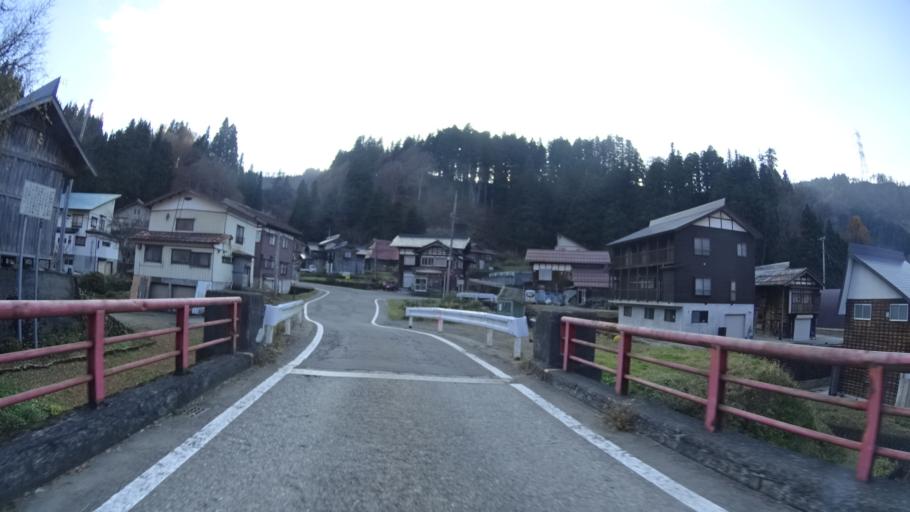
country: JP
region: Niigata
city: Shiozawa
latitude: 36.9854
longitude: 138.7442
